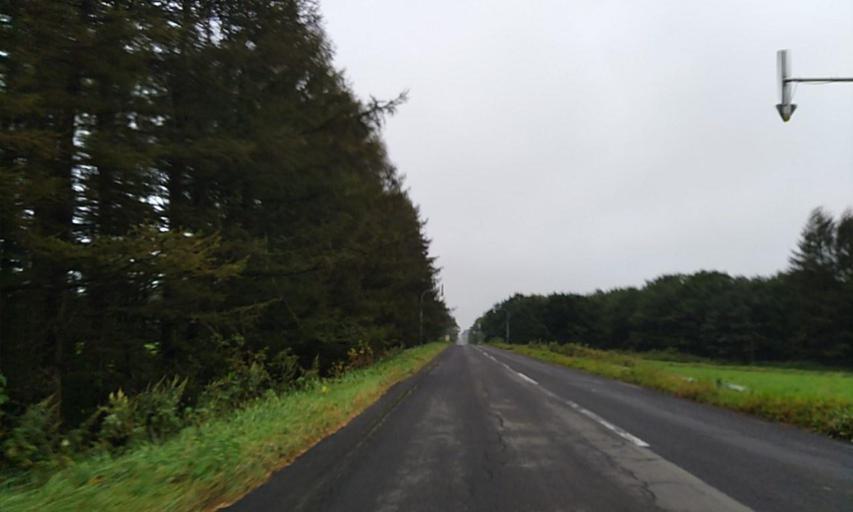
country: JP
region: Hokkaido
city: Shibetsu
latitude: 43.5212
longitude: 144.6862
